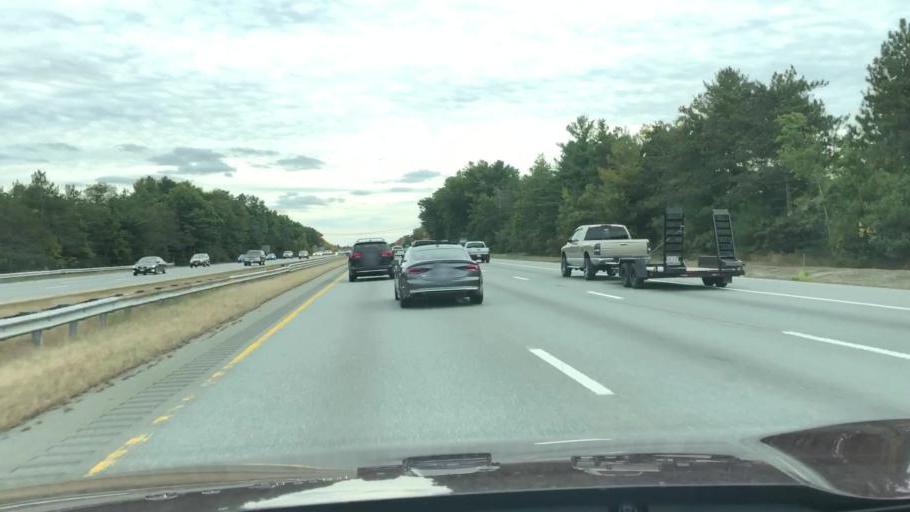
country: US
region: Massachusetts
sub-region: Middlesex County
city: Tewksbury
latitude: 42.6086
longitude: -71.1732
